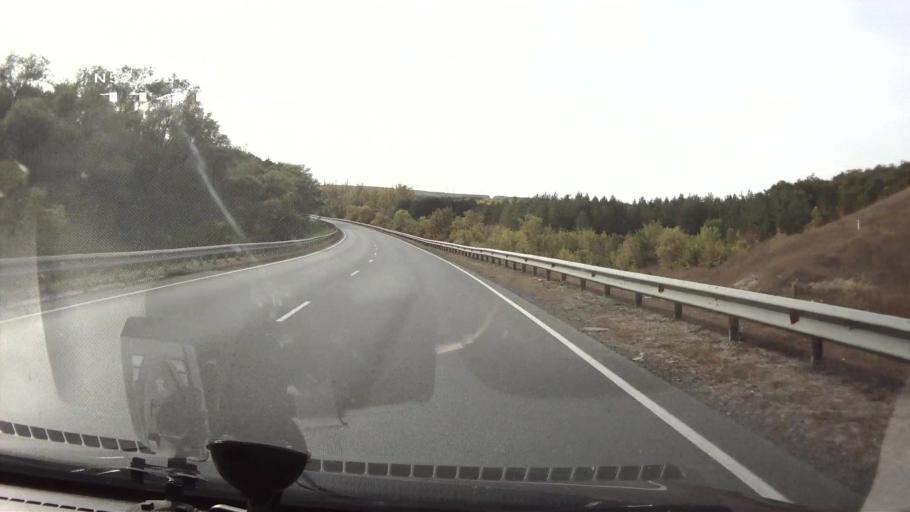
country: RU
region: Saratov
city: Tersa
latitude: 52.1037
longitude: 47.4882
